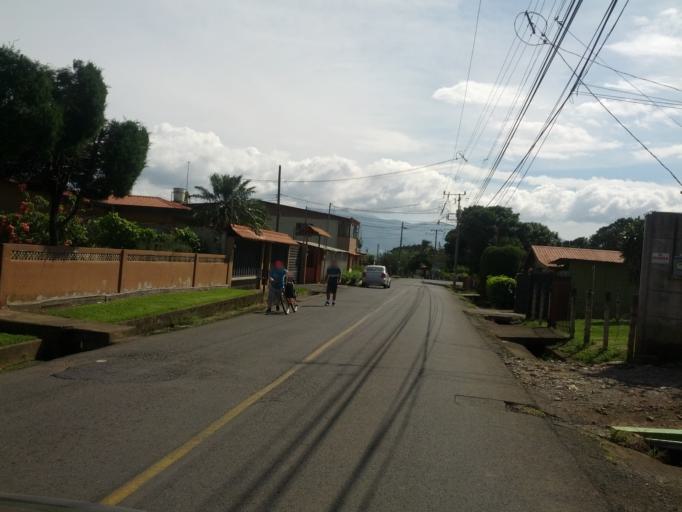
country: CR
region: Heredia
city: Llorente
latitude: 10.0234
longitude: -84.1763
